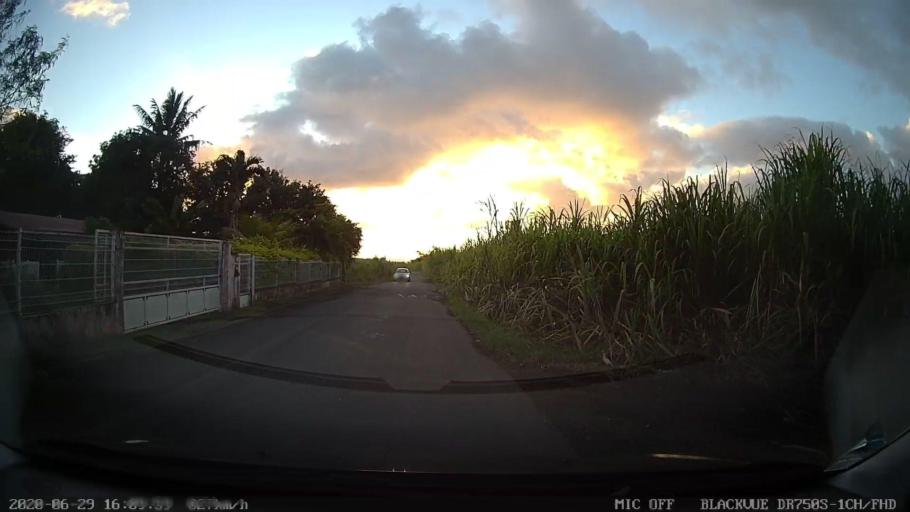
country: RE
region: Reunion
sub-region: Reunion
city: Bras-Panon
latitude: -20.9916
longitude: 55.6849
